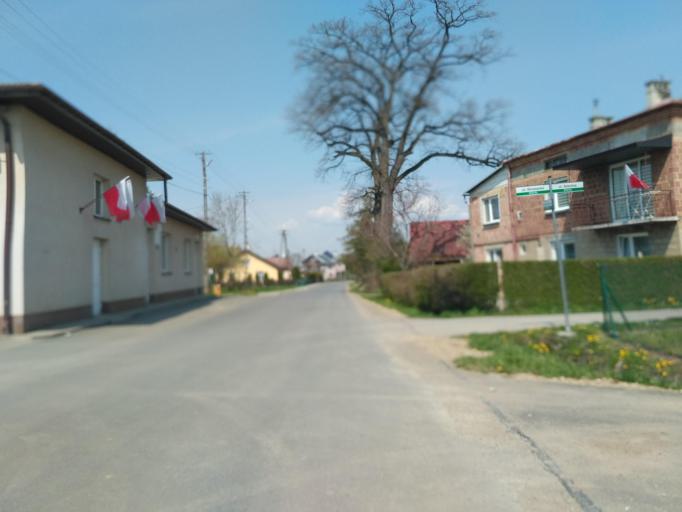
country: PL
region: Subcarpathian Voivodeship
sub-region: Powiat krosnienski
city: Chorkowka
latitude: 49.6303
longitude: 21.7012
